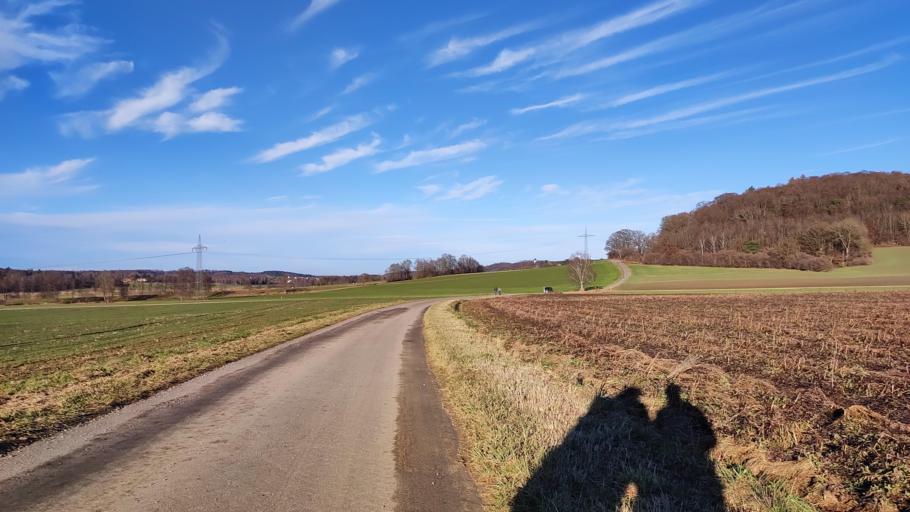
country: DE
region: Bavaria
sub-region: Swabia
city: Zusmarshausen
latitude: 48.3849
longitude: 10.5897
